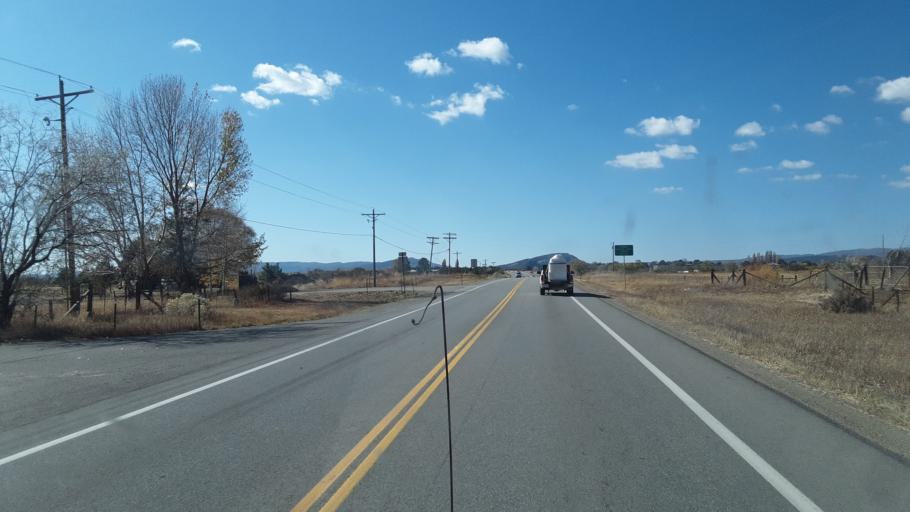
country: US
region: Colorado
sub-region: La Plata County
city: Durango
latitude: 37.2298
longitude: -107.7888
